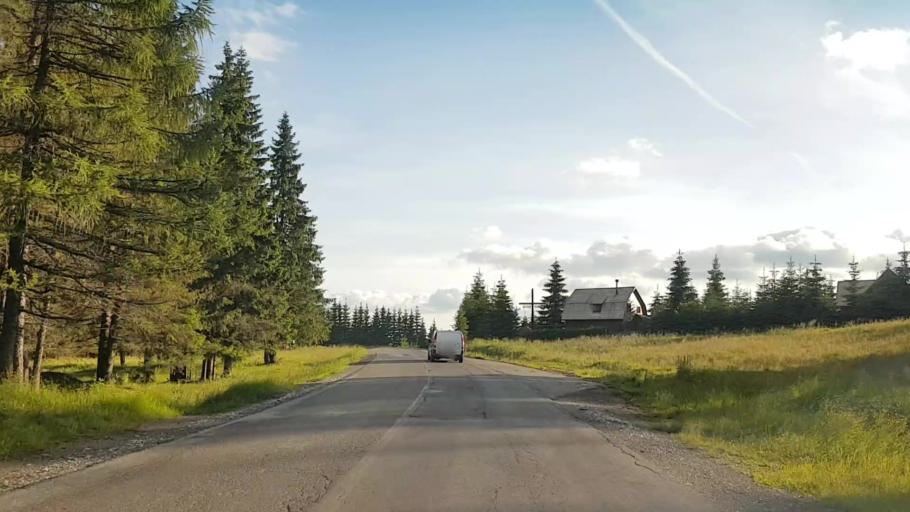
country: RO
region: Harghita
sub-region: Comuna Varsag
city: Varsag
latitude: 46.6564
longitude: 25.2974
